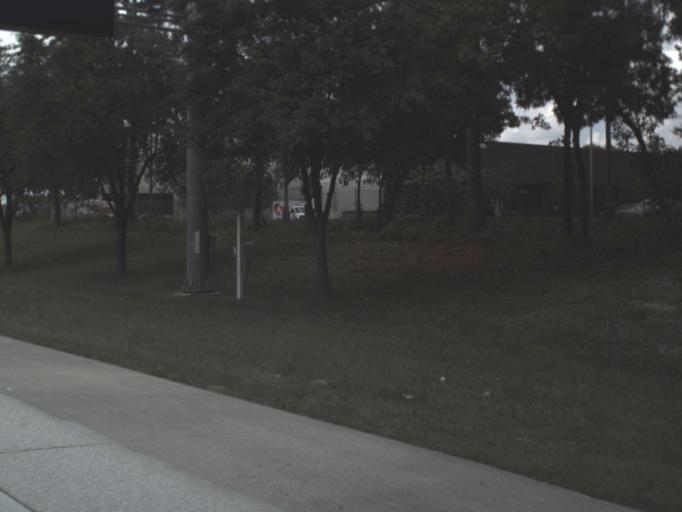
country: US
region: Florida
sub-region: Saint Johns County
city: Fruit Cove
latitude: 30.2025
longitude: -81.5590
